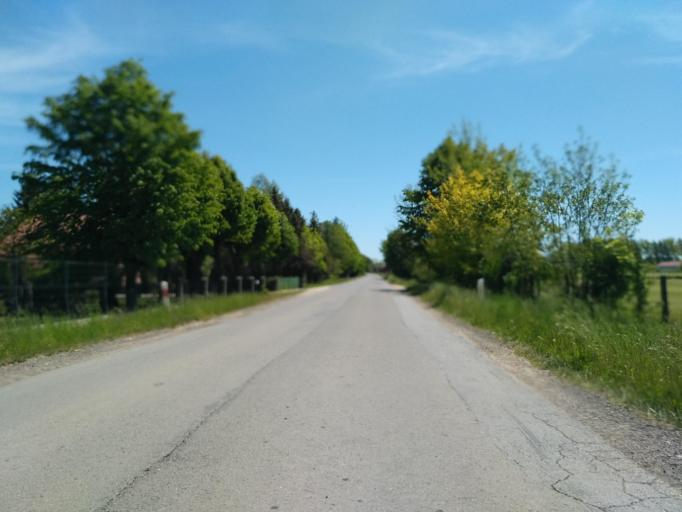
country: PL
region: Subcarpathian Voivodeship
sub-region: Powiat krosnienski
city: Sieniawa
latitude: 49.5427
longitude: 21.9580
